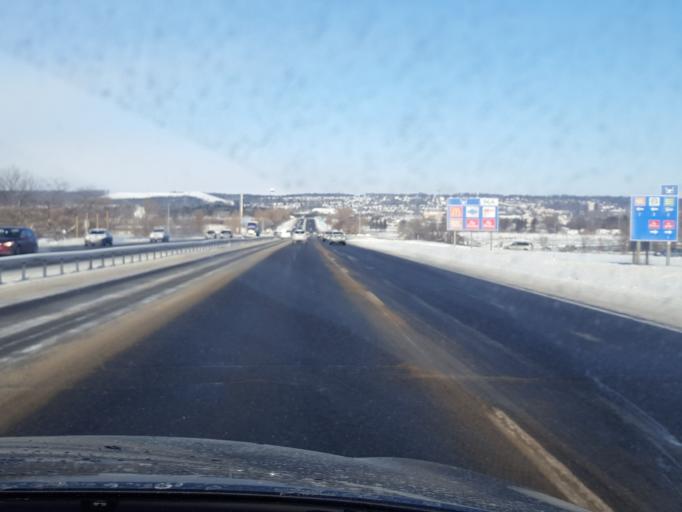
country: CA
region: Ontario
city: Barrie
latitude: 44.3602
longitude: -79.6951
